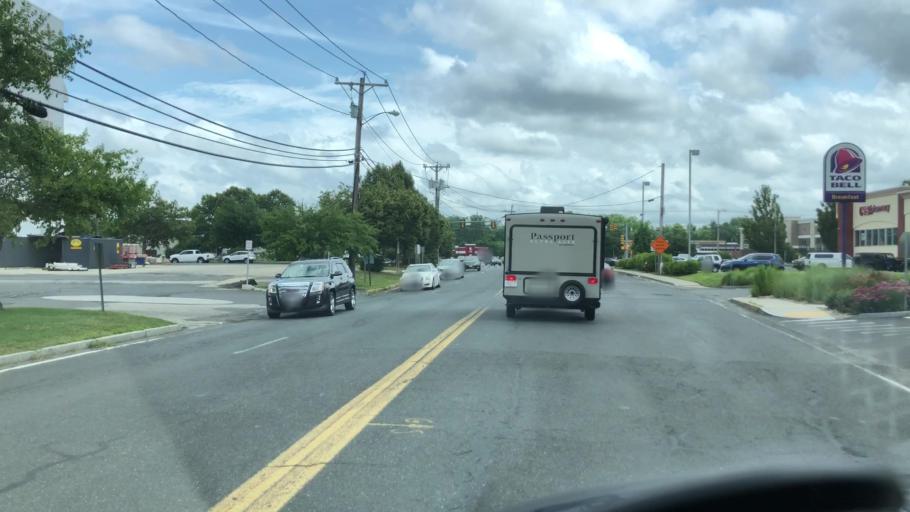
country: US
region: Massachusetts
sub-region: Hampden County
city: West Springfield
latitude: 42.1298
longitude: -72.6281
